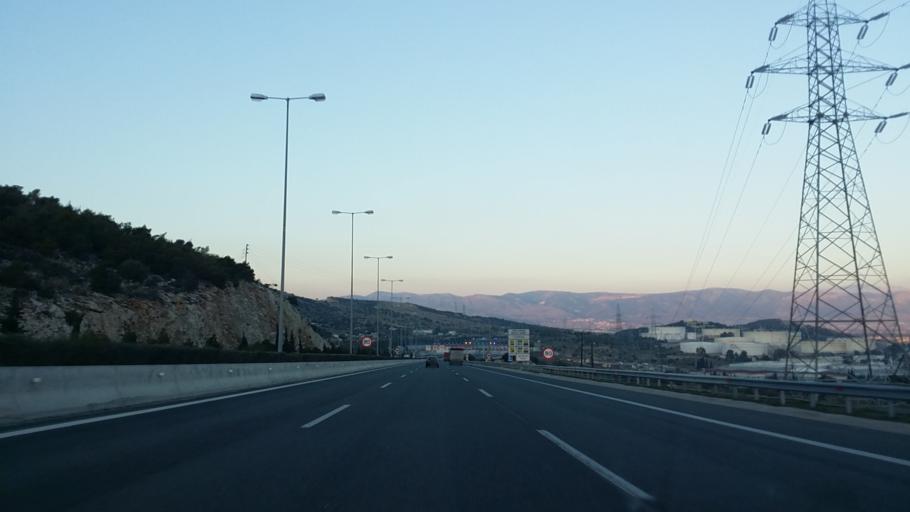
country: GR
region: Attica
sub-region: Nomarchia Dytikis Attikis
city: Mandra
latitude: 38.0333
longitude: 23.4902
